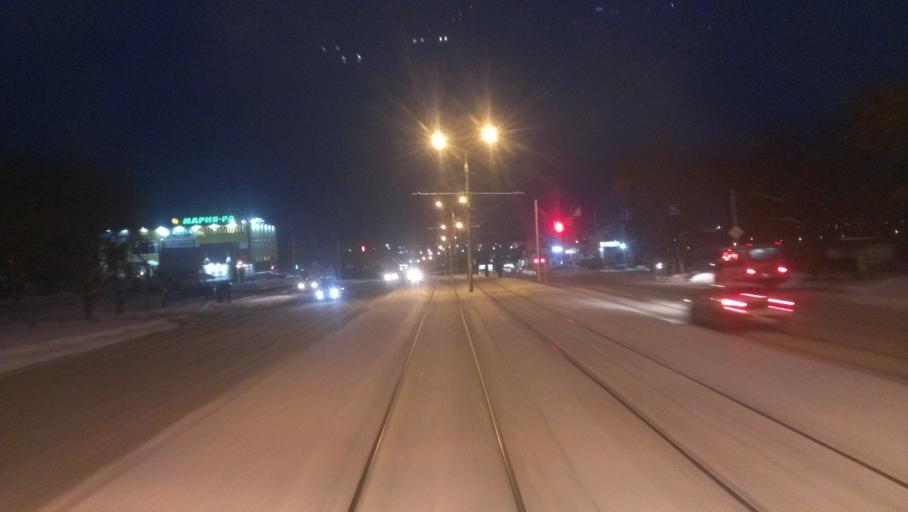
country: RU
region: Altai Krai
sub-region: Gorod Barnaulskiy
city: Barnaul
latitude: 53.3763
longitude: 83.6799
